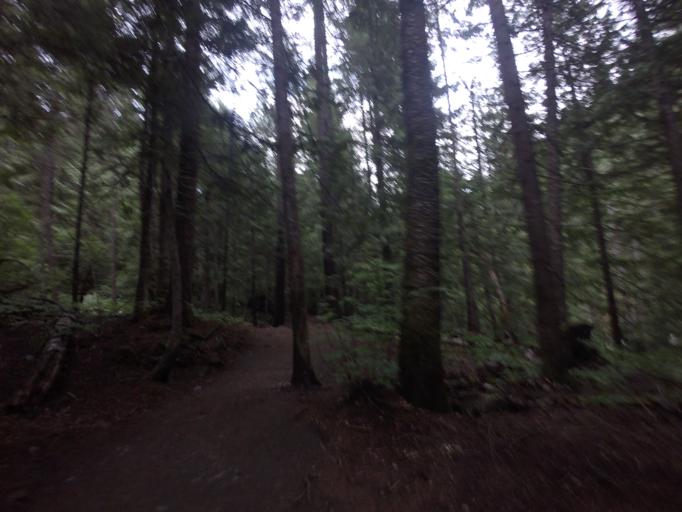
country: CA
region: British Columbia
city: Pemberton
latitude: 50.2909
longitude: -122.8313
